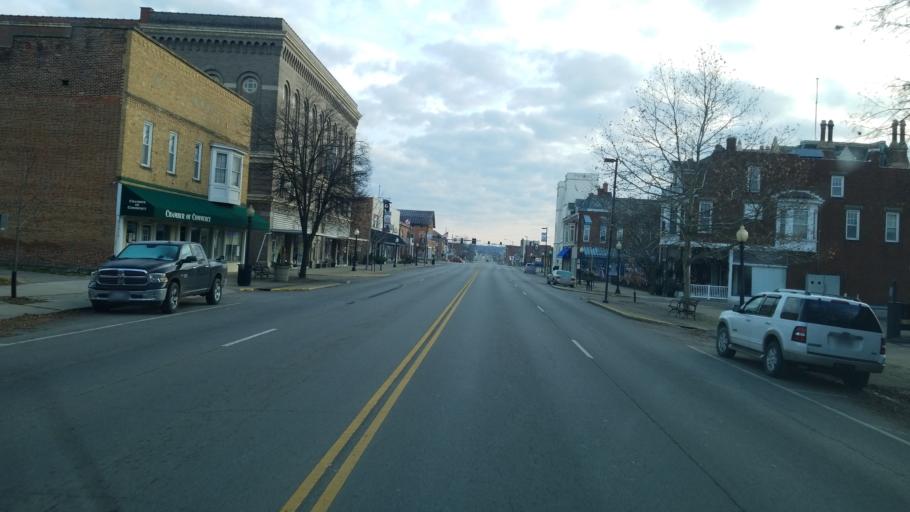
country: US
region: Ohio
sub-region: Ross County
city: Chillicothe
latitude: 39.3331
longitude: -82.9813
